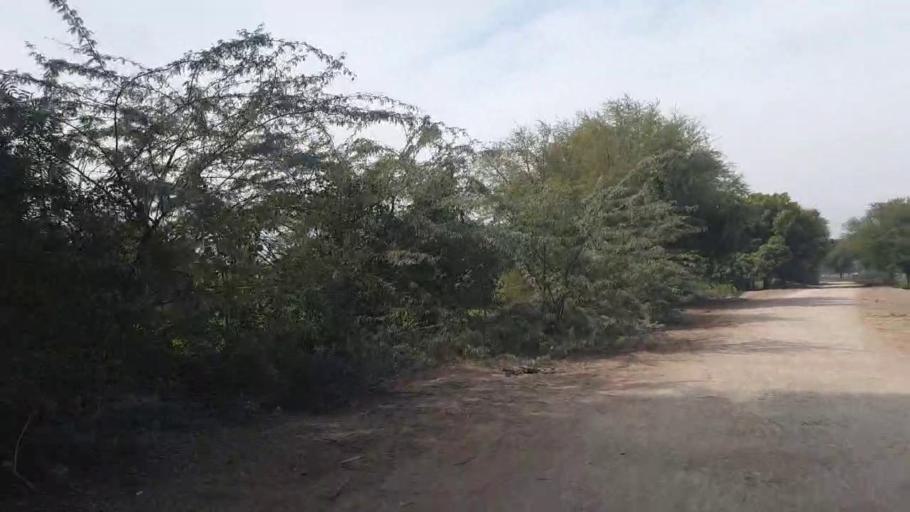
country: PK
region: Sindh
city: Nawabshah
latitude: 26.1194
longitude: 68.4750
